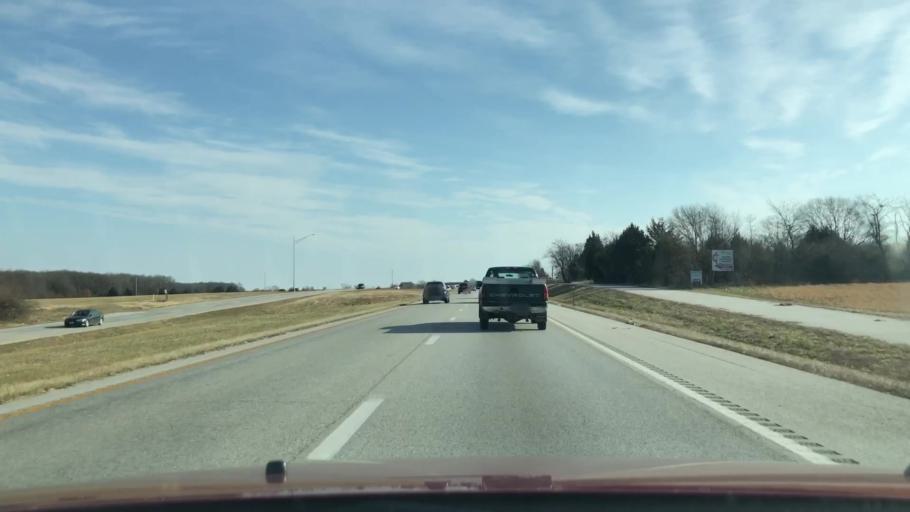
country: US
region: Missouri
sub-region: Webster County
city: Rogersville
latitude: 37.1181
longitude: -93.0975
